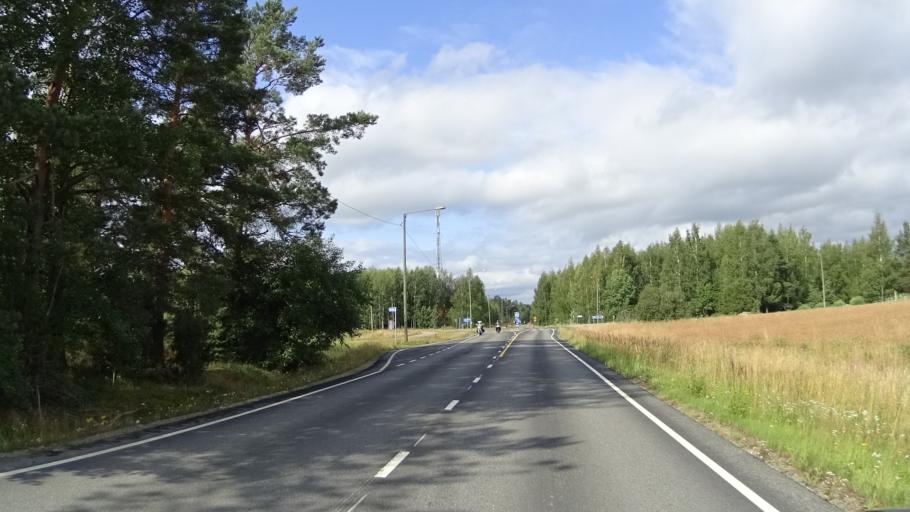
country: FI
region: Pirkanmaa
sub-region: Tampere
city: Luopioinen
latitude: 61.4828
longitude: 24.7076
